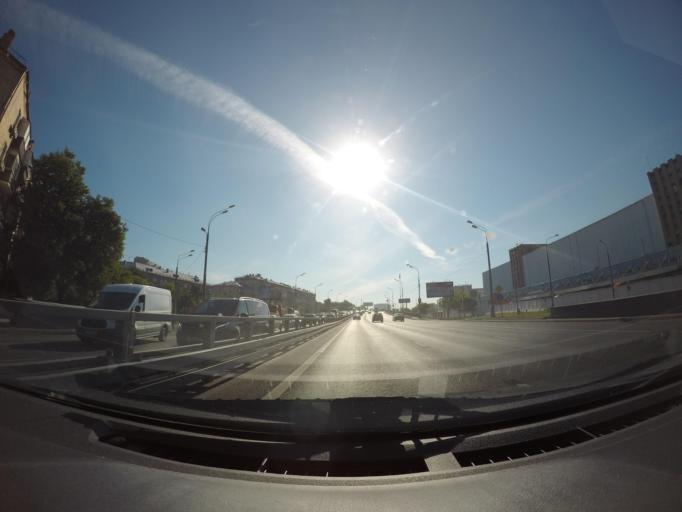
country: RU
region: Moscow
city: Ryazanskiy
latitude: 55.7298
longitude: 37.7470
